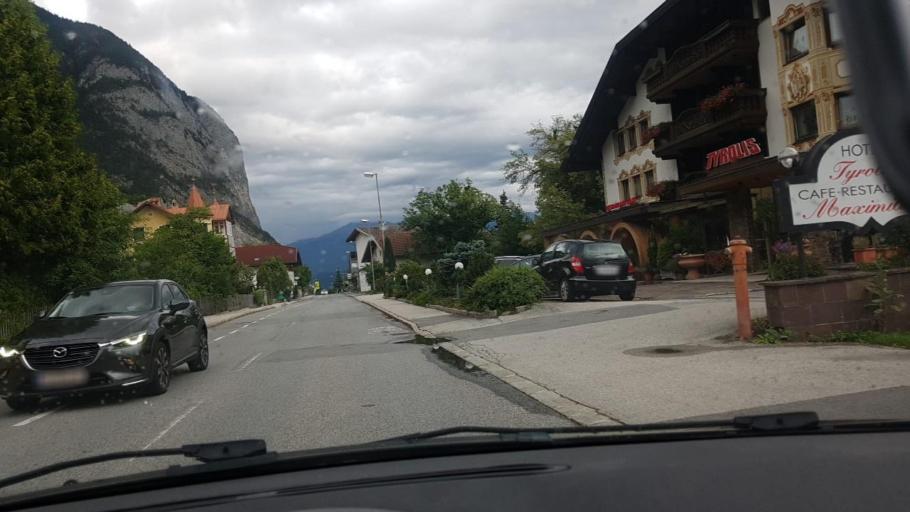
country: AT
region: Tyrol
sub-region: Politischer Bezirk Innsbruck Land
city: Unterperfuss
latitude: 47.2720
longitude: 11.2479
